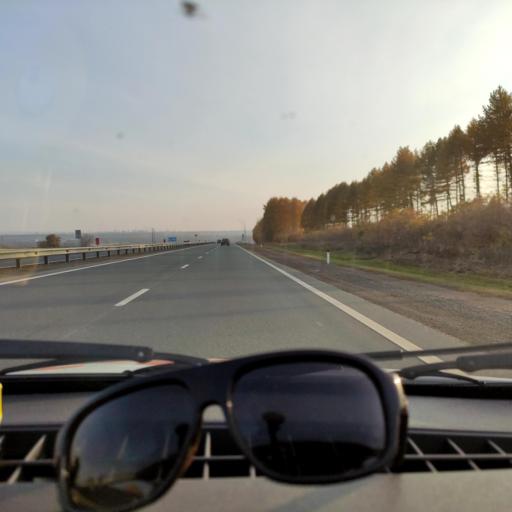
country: RU
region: Bashkortostan
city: Sterlitamak
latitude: 53.7587
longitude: 55.9444
